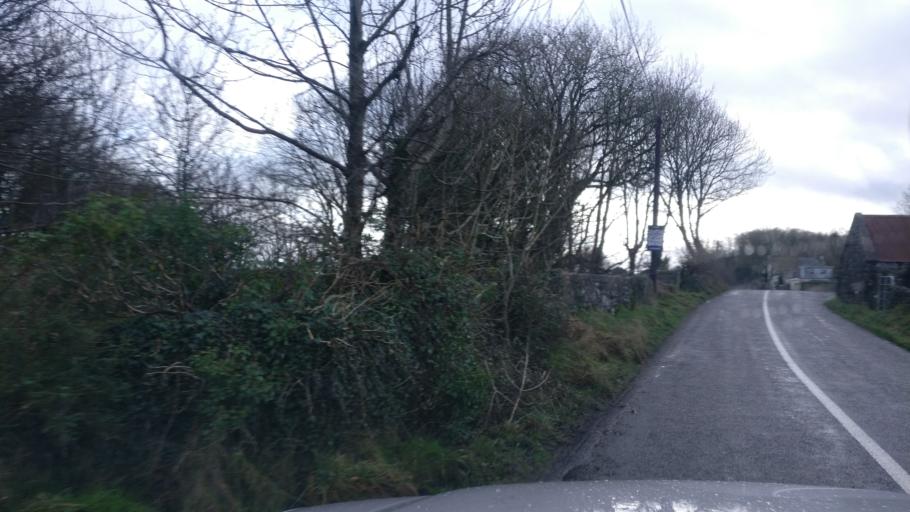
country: IE
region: Connaught
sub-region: County Galway
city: Loughrea
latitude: 53.2589
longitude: -8.6262
